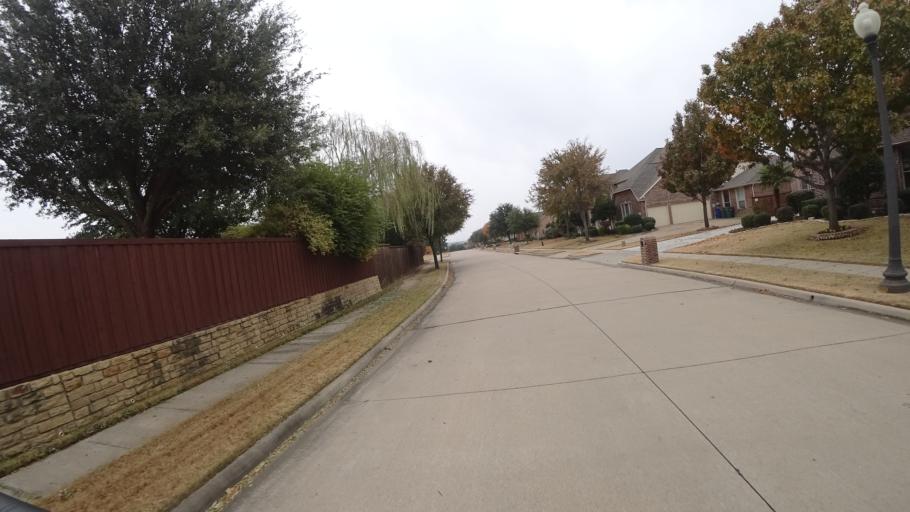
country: US
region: Texas
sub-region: Denton County
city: Lewisville
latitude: 33.0323
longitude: -96.9323
